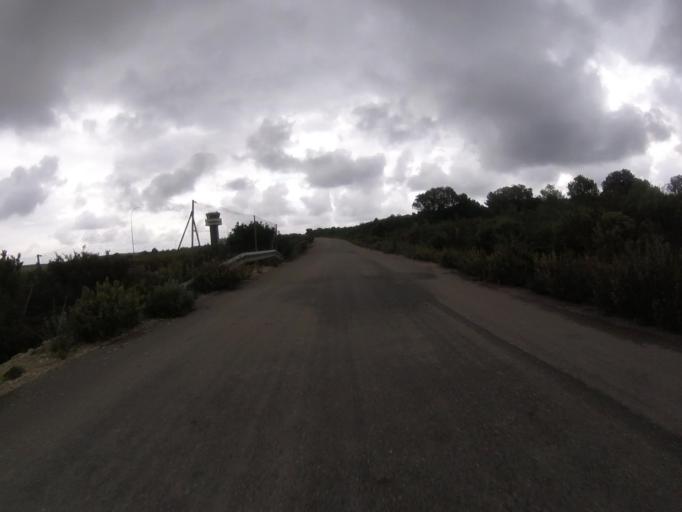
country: ES
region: Valencia
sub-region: Provincia de Castello
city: Benlloch
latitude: 40.2104
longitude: 0.0764
